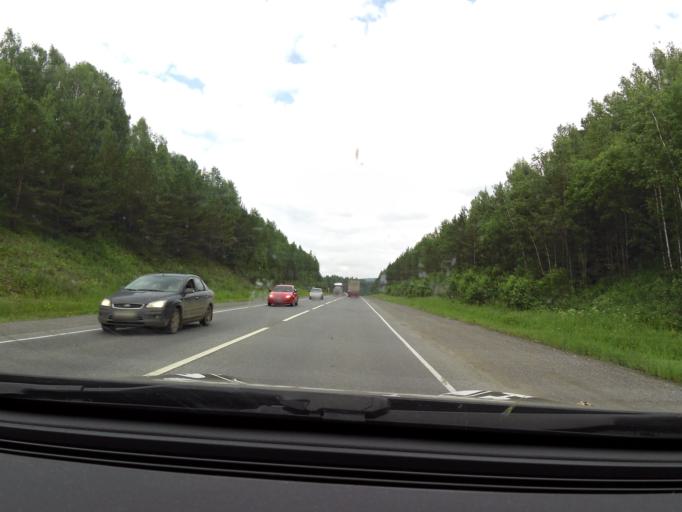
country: RU
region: Sverdlovsk
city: Druzhinino
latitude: 56.8341
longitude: 59.6359
